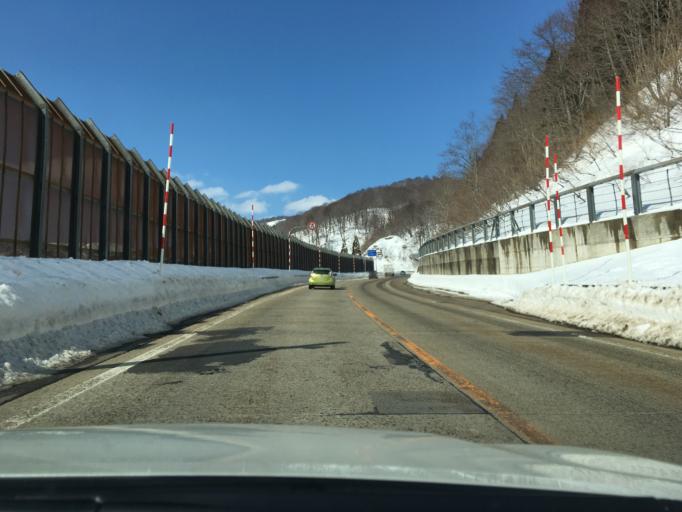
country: JP
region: Yamagata
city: Tsuruoka
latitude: 38.4844
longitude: 139.9901
